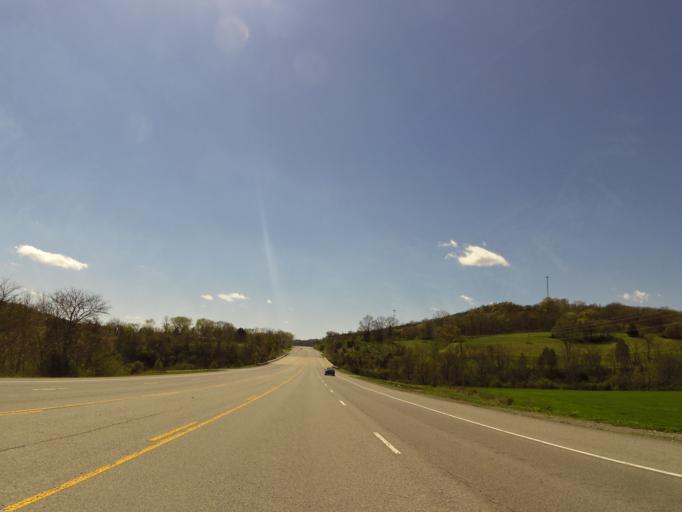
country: US
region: Tennessee
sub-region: DeKalb County
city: Smithville
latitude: 36.0113
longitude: -85.9635
